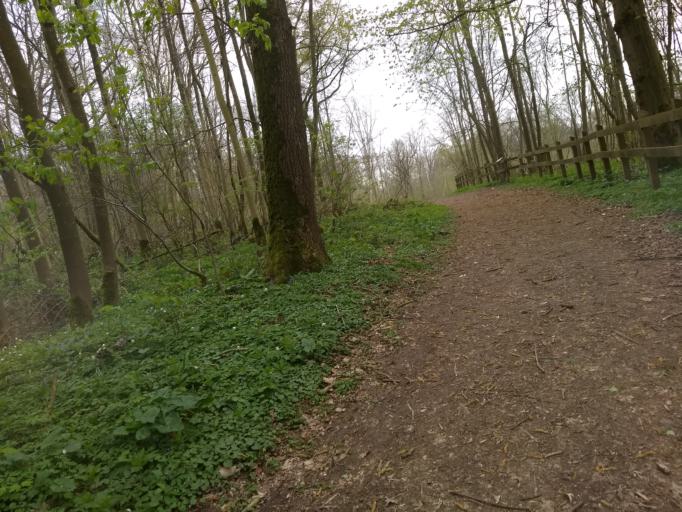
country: FR
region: Nord-Pas-de-Calais
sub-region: Departement du Pas-de-Calais
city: Maroeuil
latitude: 50.3326
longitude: 2.6930
